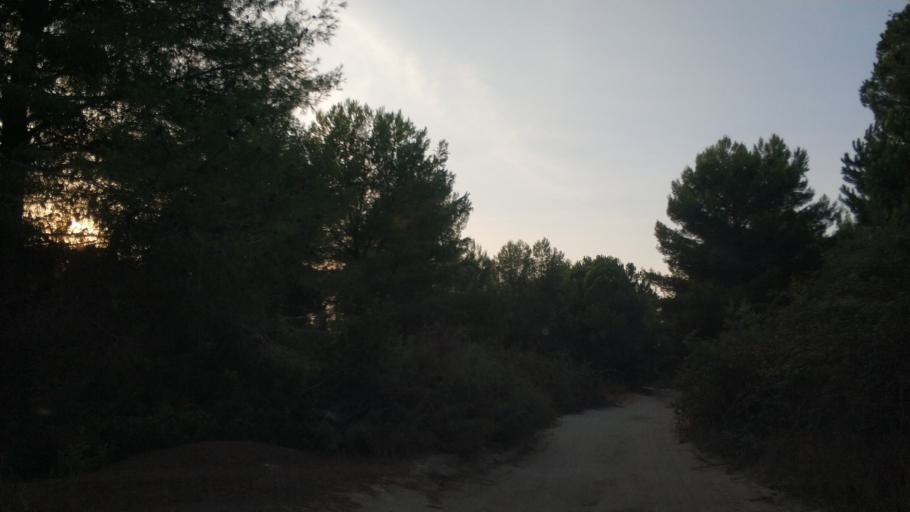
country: AL
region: Fier
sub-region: Rrethi i Lushnjes
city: Divjake
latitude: 40.9525
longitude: 19.4754
